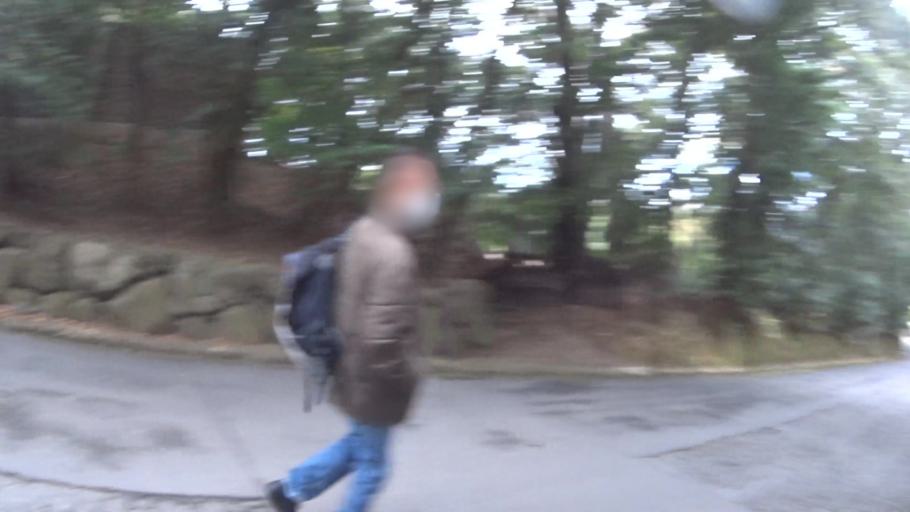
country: JP
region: Kyoto
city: Kyoto
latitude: 34.9785
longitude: 135.7790
